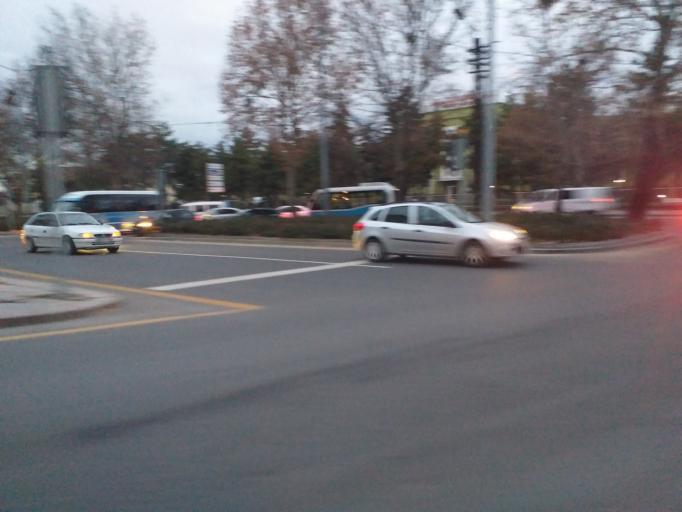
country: TR
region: Ankara
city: Ankara
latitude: 39.9439
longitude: 32.8248
